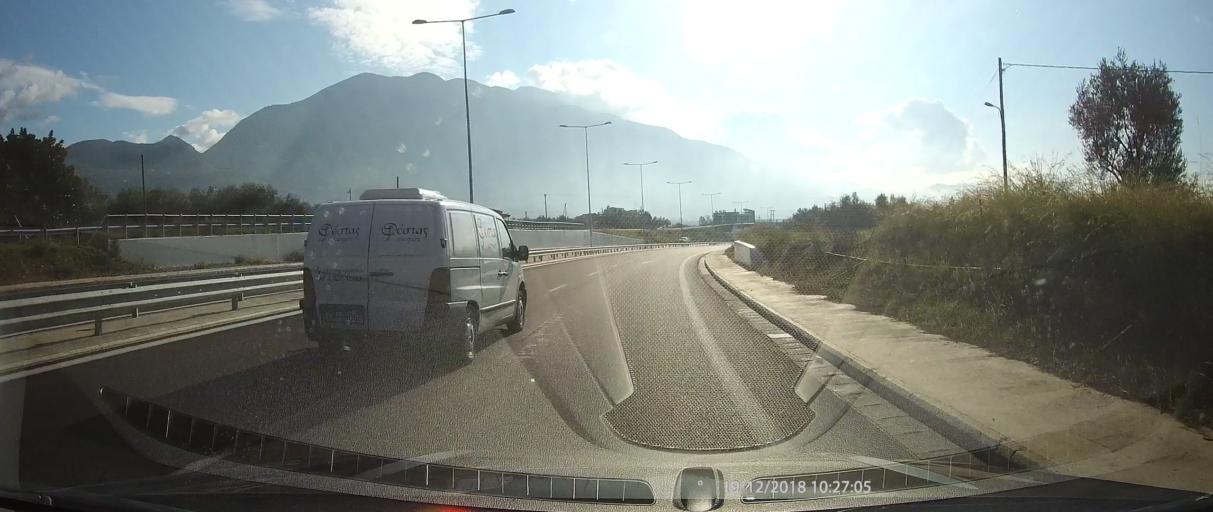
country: GR
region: Peloponnese
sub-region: Nomos Messinias
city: Kalamata
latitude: 37.0403
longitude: 22.1340
